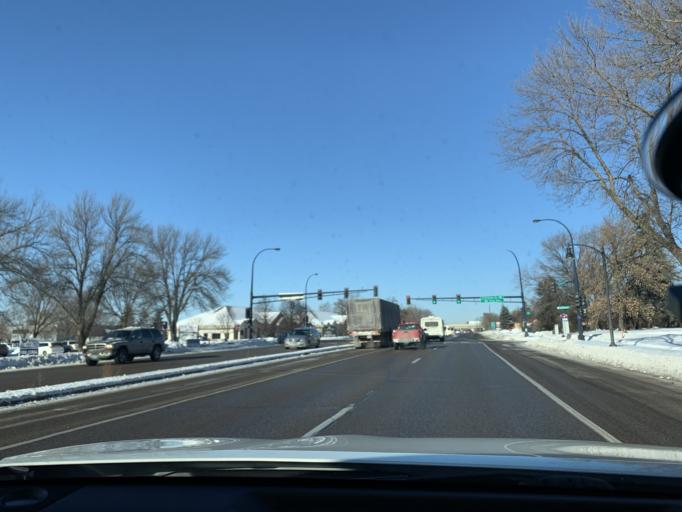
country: US
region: Minnesota
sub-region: Anoka County
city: Coon Rapids
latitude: 45.1391
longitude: -93.2744
